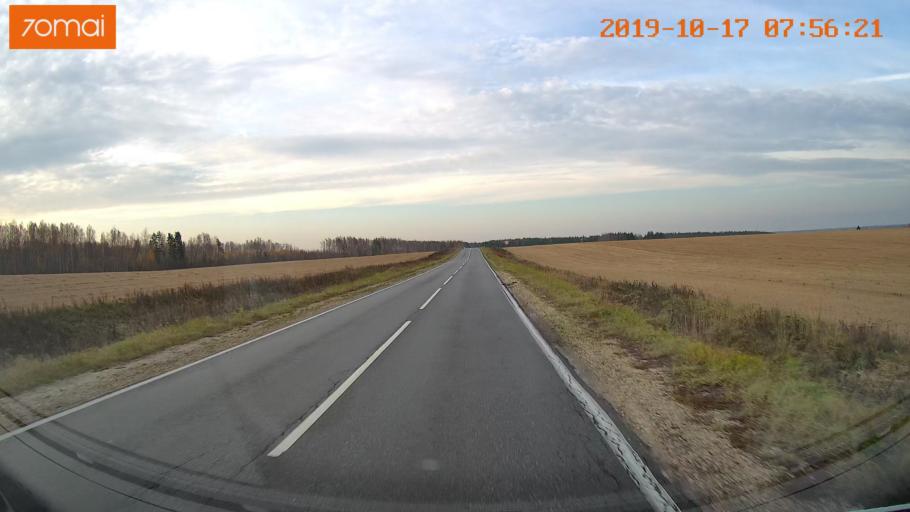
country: RU
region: Vladimir
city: Bavleny
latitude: 56.4242
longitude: 39.5915
